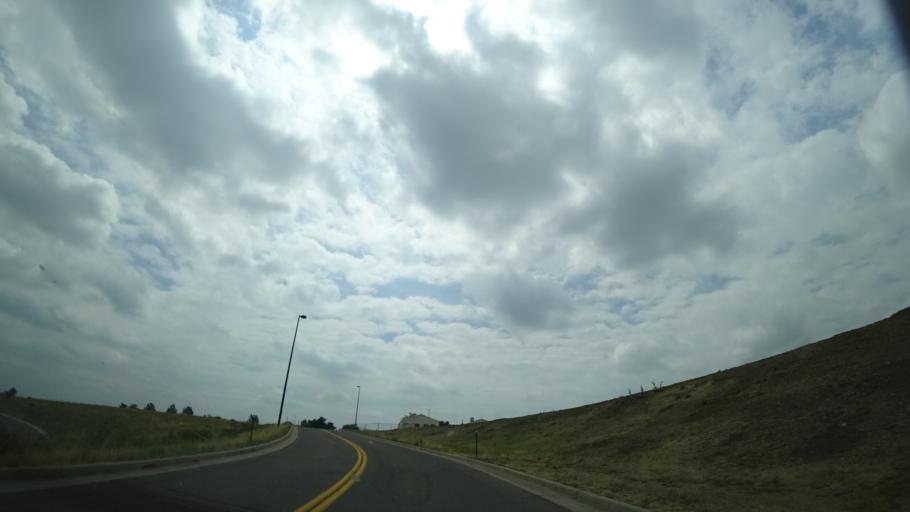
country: US
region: Colorado
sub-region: Jefferson County
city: West Pleasant View
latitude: 39.7144
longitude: -105.1534
